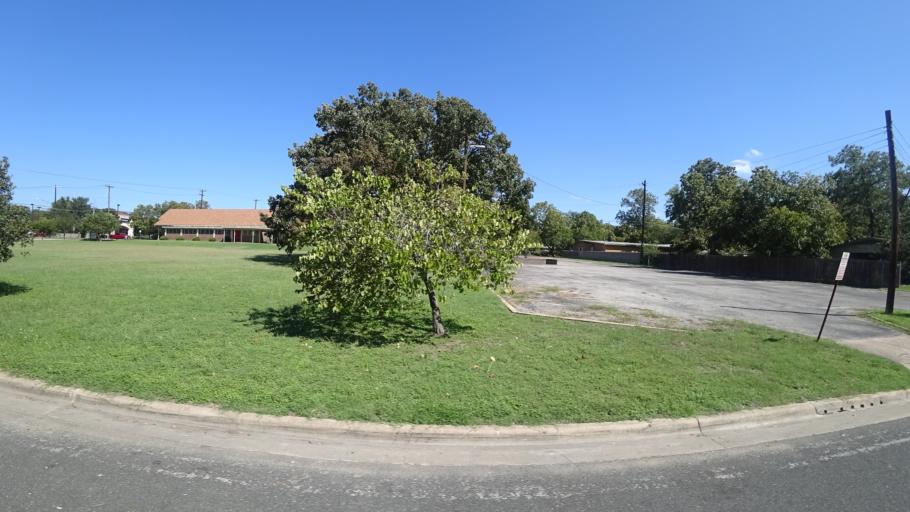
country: US
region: Texas
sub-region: Travis County
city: Austin
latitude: 30.3148
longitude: -97.7014
